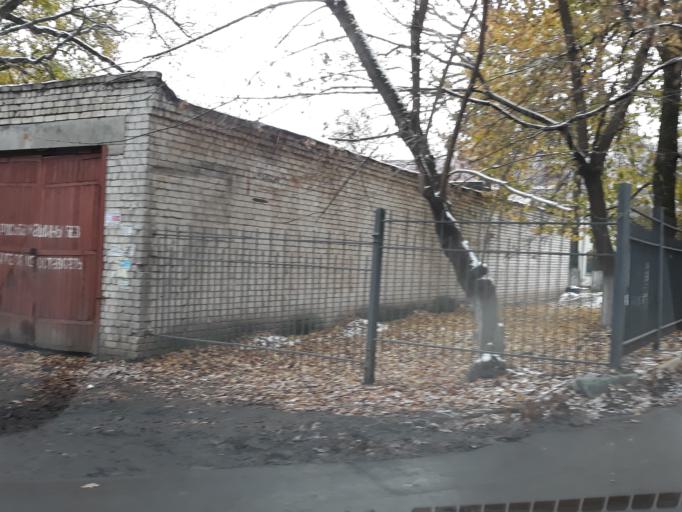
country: RU
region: Nizjnij Novgorod
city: Nizhniy Novgorod
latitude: 56.2591
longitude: 43.9751
